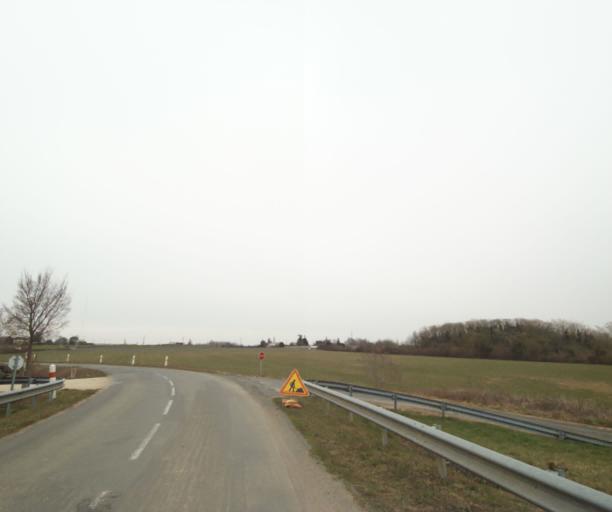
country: FR
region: Poitou-Charentes
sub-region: Departement des Deux-Sevres
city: Bessines
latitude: 46.3445
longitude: -0.5112
